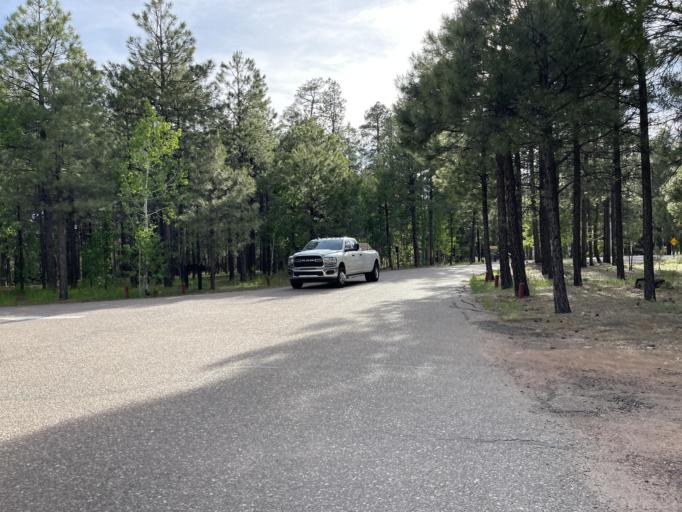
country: US
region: Arizona
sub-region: Navajo County
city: Heber-Overgaard
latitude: 34.3247
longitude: -110.8269
